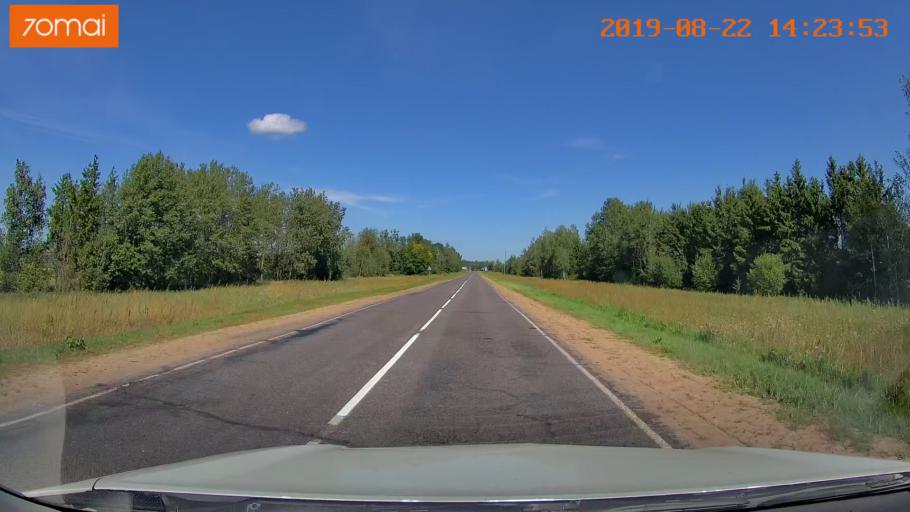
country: BY
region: Mogilev
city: Asipovichy
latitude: 53.2938
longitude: 28.5908
